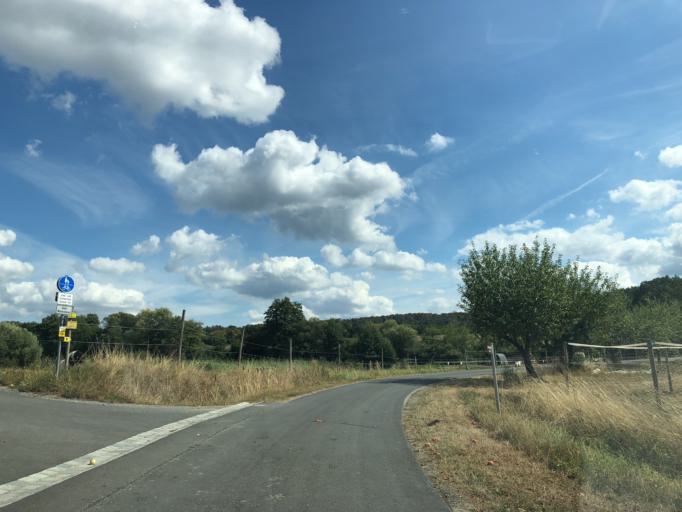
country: DE
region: Bavaria
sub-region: Regierungsbezirk Unterfranken
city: Oberschwarzach
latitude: 49.8468
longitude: 10.4316
